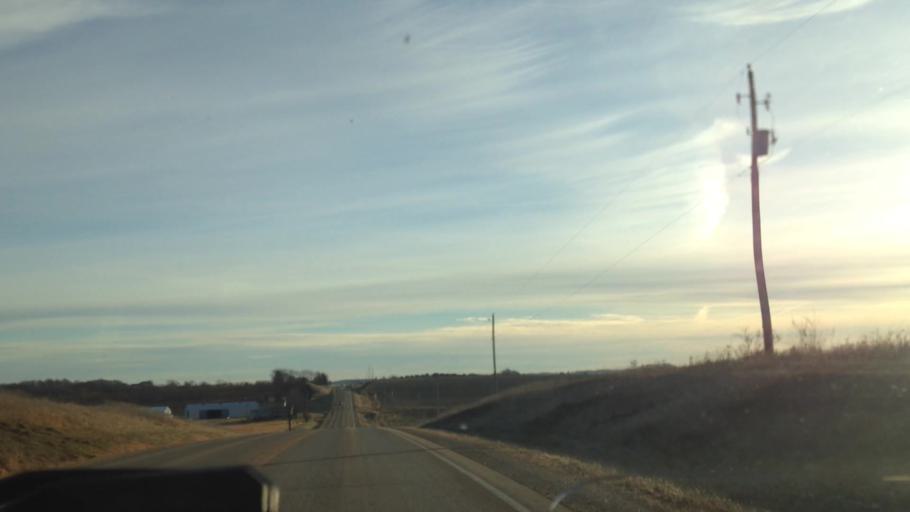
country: US
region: Wisconsin
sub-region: Dodge County
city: Theresa
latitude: 43.5363
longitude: -88.4660
